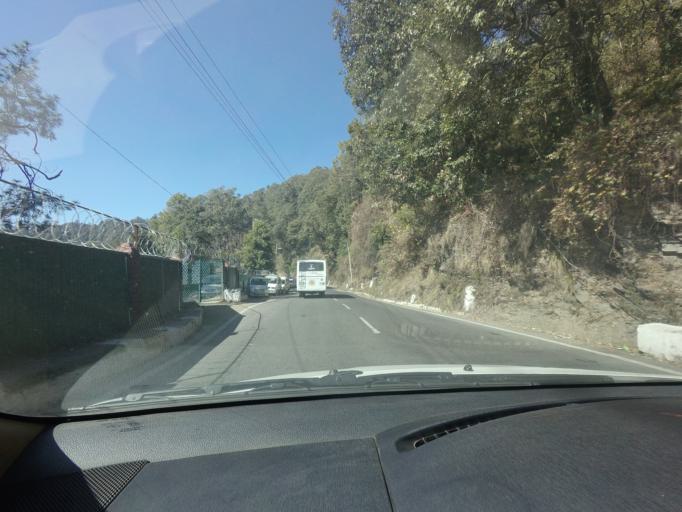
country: IN
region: Himachal Pradesh
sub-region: Shimla
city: Shimla
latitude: 31.1013
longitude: 77.1478
